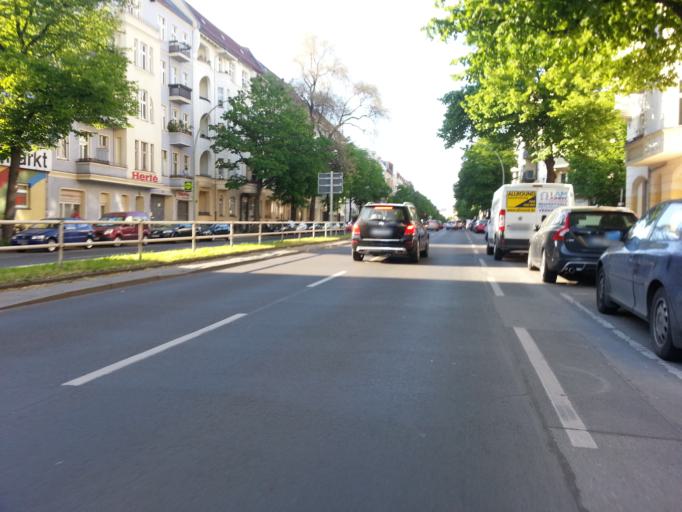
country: DE
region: Berlin
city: Charlottenburg Bezirk
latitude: 52.5123
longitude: 13.3016
